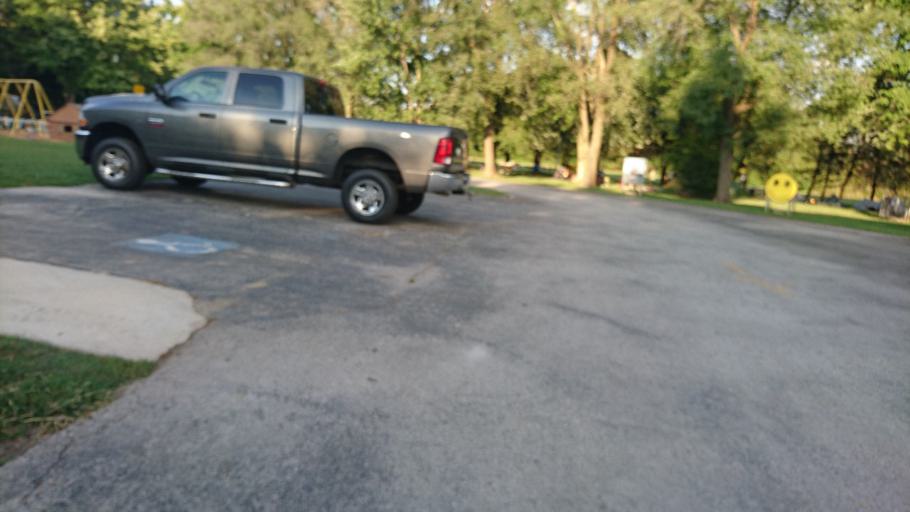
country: US
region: Missouri
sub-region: Greene County
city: Battlefield
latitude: 37.1987
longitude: -93.4022
